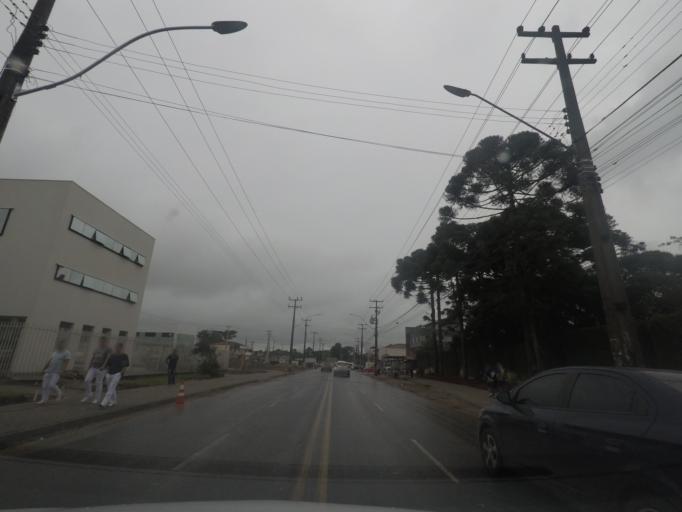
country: BR
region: Parana
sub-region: Piraquara
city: Piraquara
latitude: -25.4520
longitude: -49.0707
